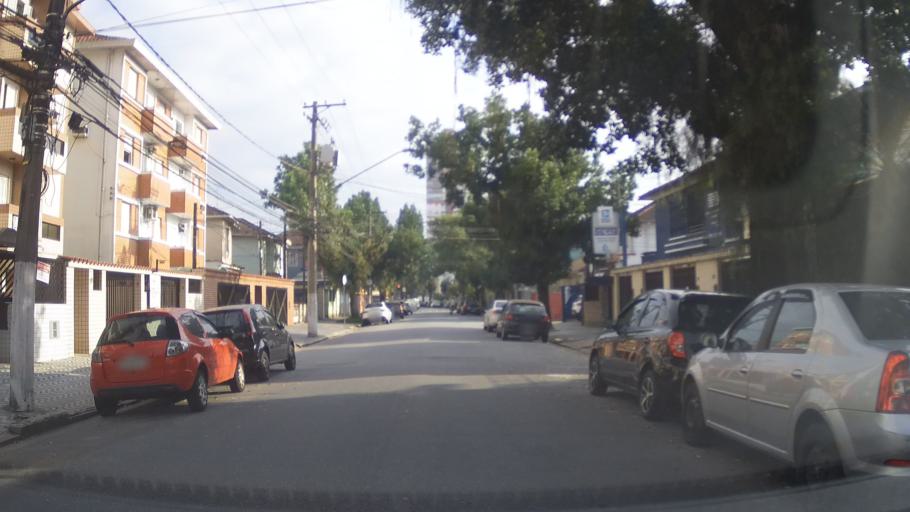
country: BR
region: Sao Paulo
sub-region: Santos
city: Santos
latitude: -23.9620
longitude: -46.3250
